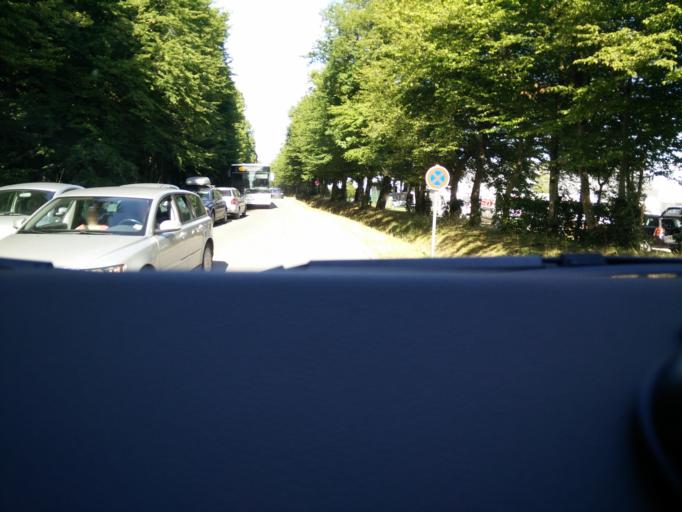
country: FR
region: Nord-Pas-de-Calais
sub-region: Departement du Nord
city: Trelon
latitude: 50.1198
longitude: 4.1396
